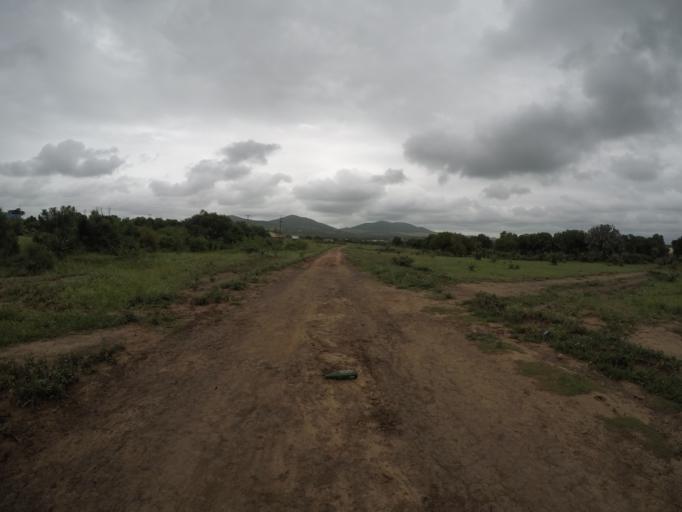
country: ZA
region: KwaZulu-Natal
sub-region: uThungulu District Municipality
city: Empangeni
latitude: -28.6078
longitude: 31.8651
